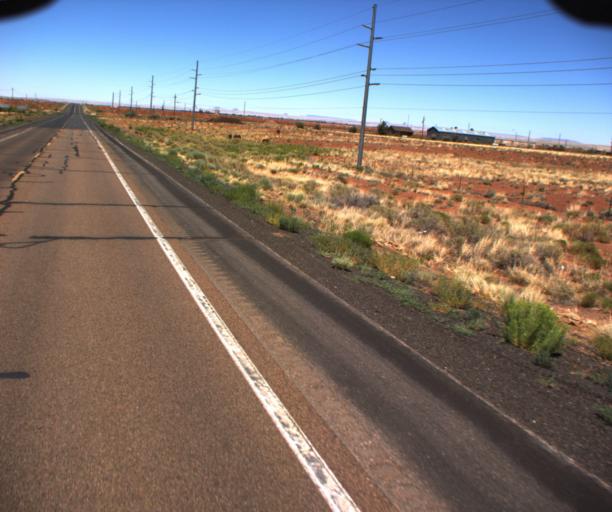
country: US
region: Arizona
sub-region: Navajo County
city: Winslow
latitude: 35.0027
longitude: -110.7047
